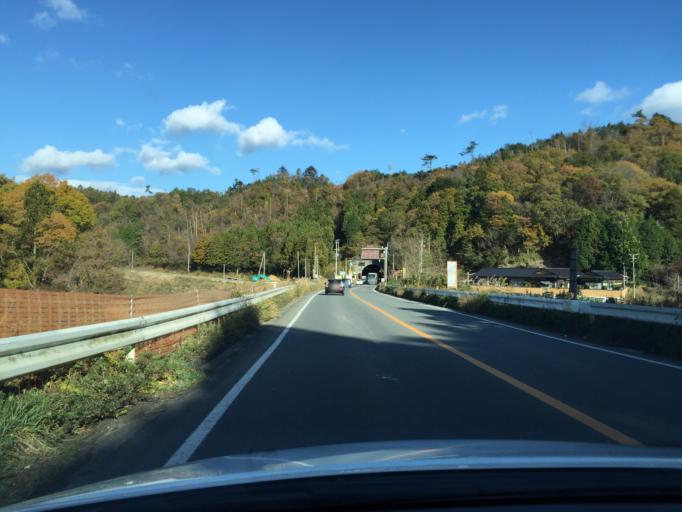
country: JP
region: Fukushima
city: Iwaki
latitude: 37.1594
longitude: 140.9953
